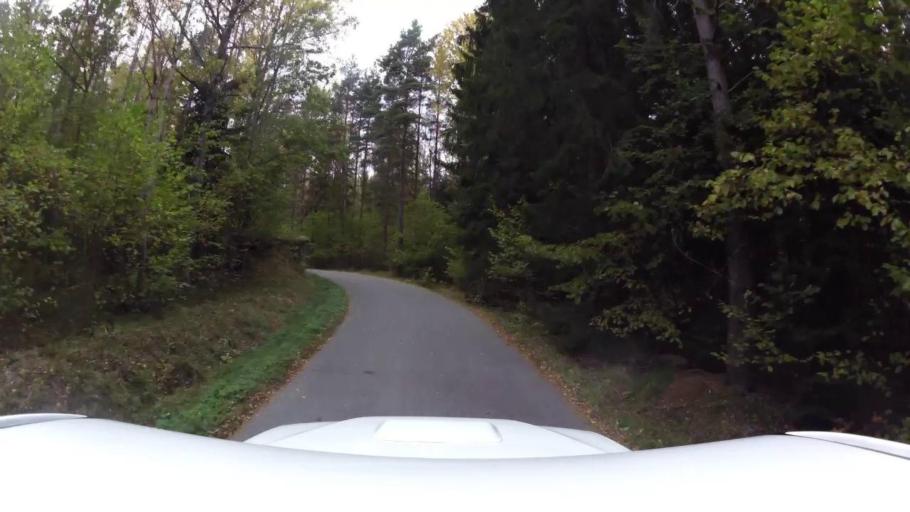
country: SE
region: OEstergoetland
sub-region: Kinda Kommun
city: Rimforsa
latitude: 58.2026
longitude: 15.5552
